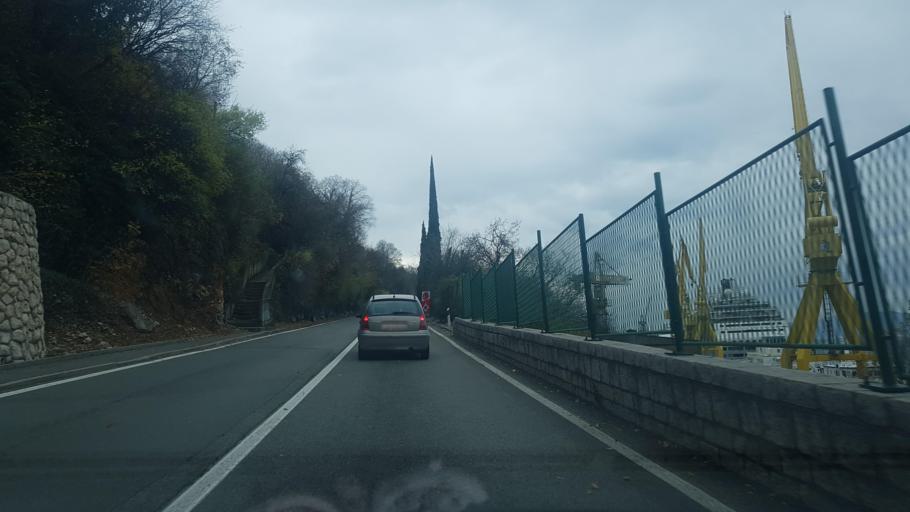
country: HR
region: Primorsko-Goranska
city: Cernik
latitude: 45.3156
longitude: 14.4844
